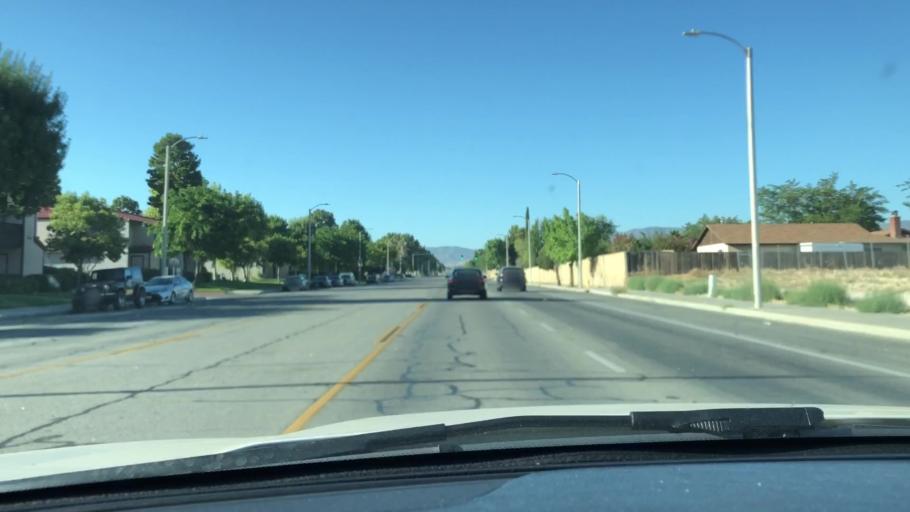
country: US
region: California
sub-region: Los Angeles County
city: Quartz Hill
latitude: 34.6699
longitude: -118.1836
